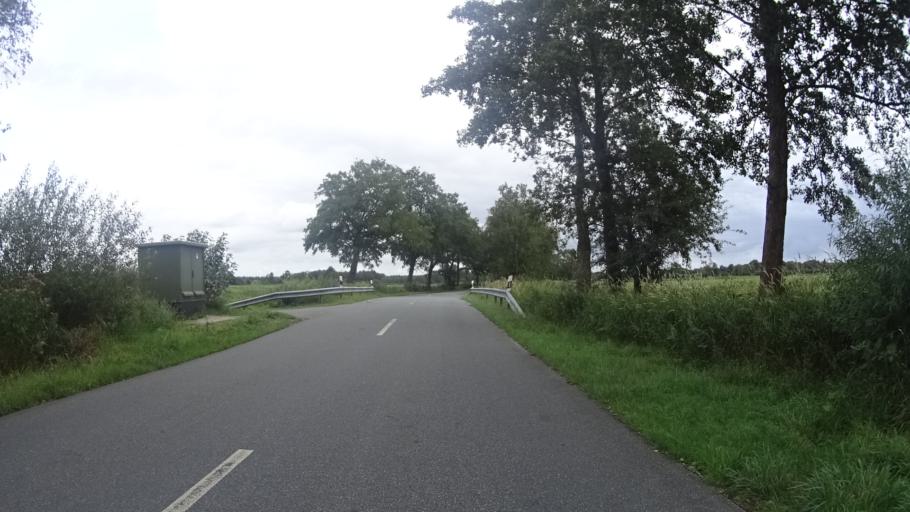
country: DE
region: Lower Saxony
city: Lintig
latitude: 53.6232
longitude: 8.8689
